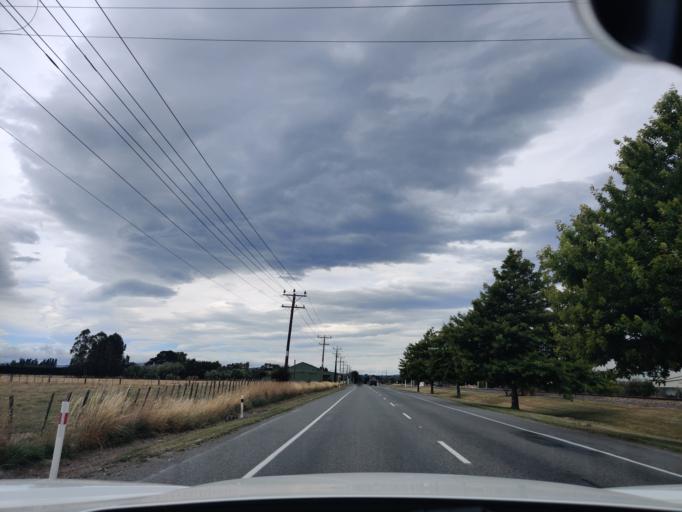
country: NZ
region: Wellington
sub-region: Masterton District
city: Masterton
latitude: -40.9551
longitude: 175.6211
